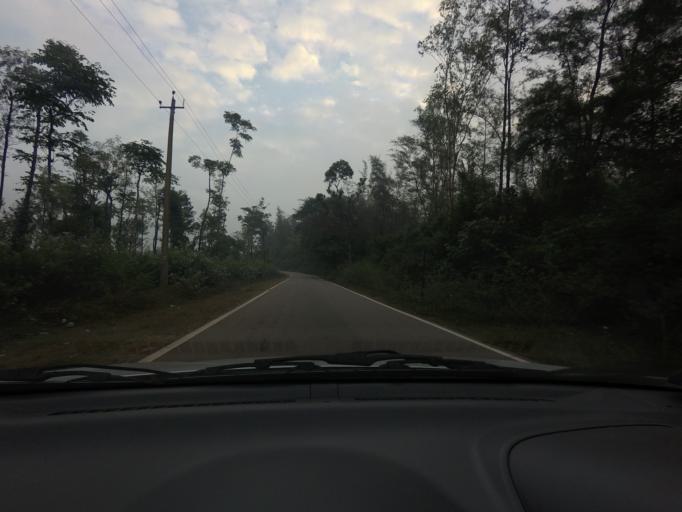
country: IN
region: Karnataka
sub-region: Hassan
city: Sakleshpur
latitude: 12.8936
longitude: 75.7590
